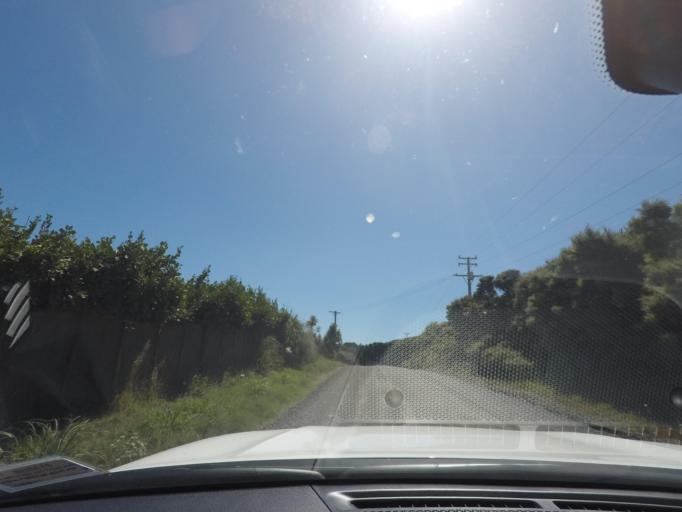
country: NZ
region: Auckland
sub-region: Auckland
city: Parakai
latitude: -36.5832
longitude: 174.3060
